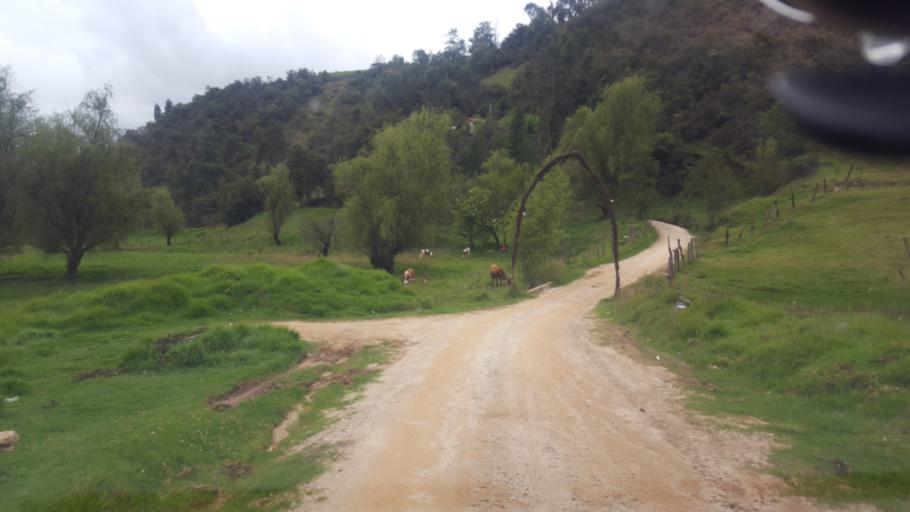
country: CO
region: Boyaca
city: Belen
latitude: 6.0149
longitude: -72.8722
